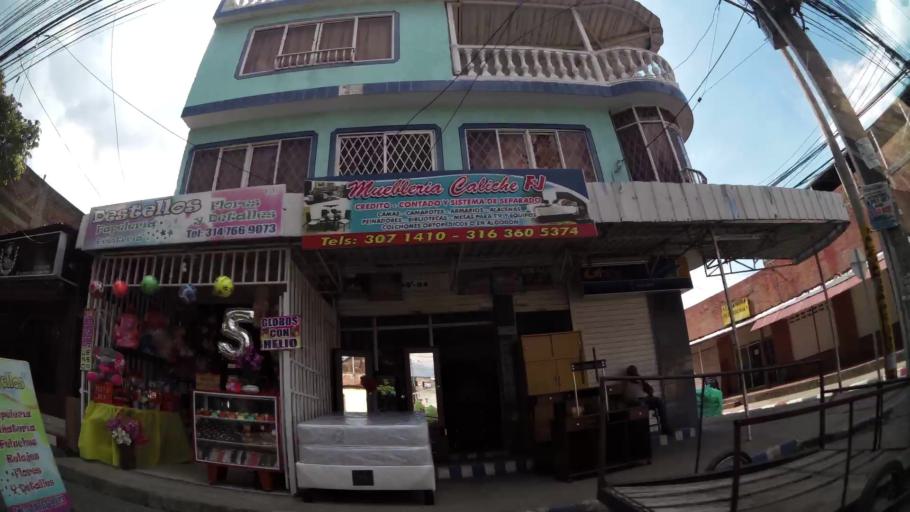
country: CO
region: Valle del Cauca
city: Cali
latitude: 3.4180
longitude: -76.5162
